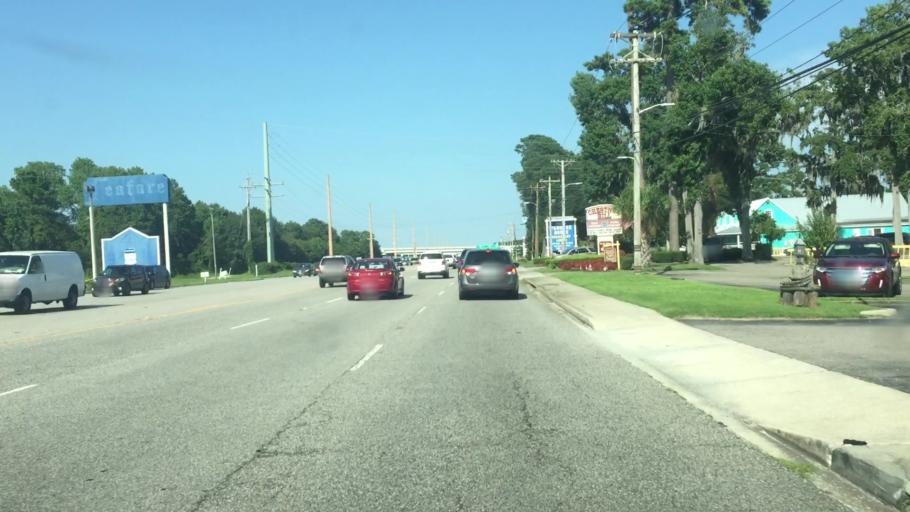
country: US
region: South Carolina
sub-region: Horry County
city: North Myrtle Beach
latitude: 33.7846
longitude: -78.7828
